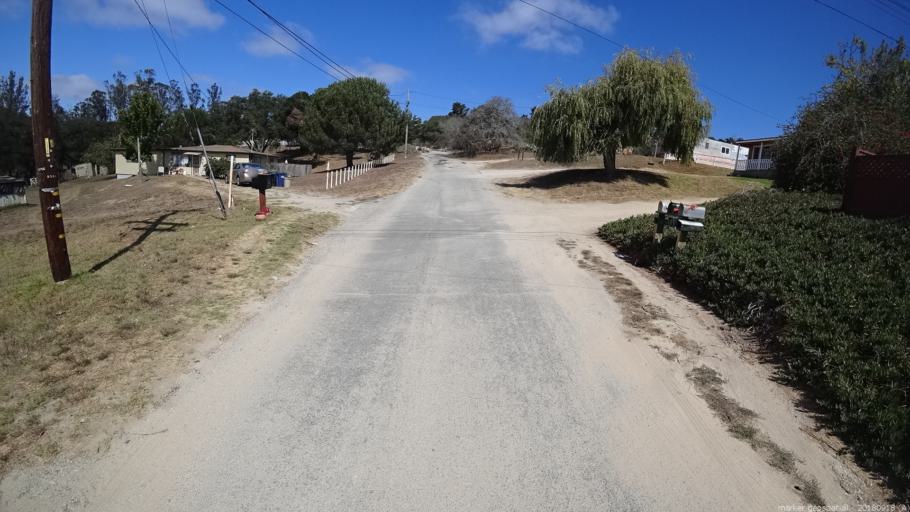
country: US
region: California
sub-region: Monterey County
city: Prunedale
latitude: 36.7818
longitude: -121.6633
